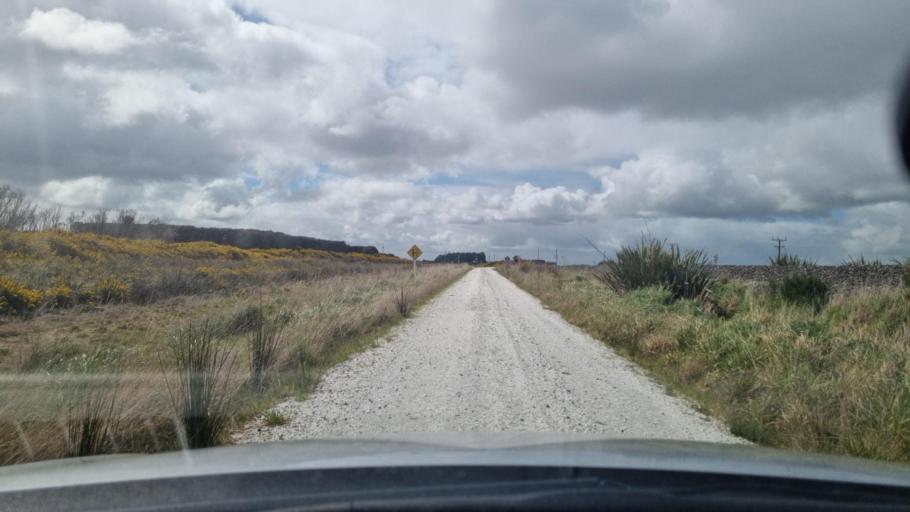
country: NZ
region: Southland
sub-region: Invercargill City
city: Bluff
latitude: -46.5289
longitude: 168.3062
